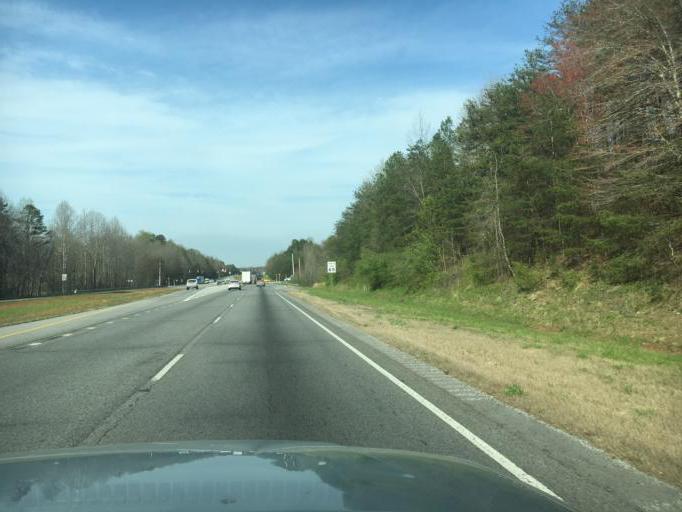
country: US
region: Georgia
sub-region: Banks County
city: Alto
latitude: 34.4953
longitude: -83.5767
